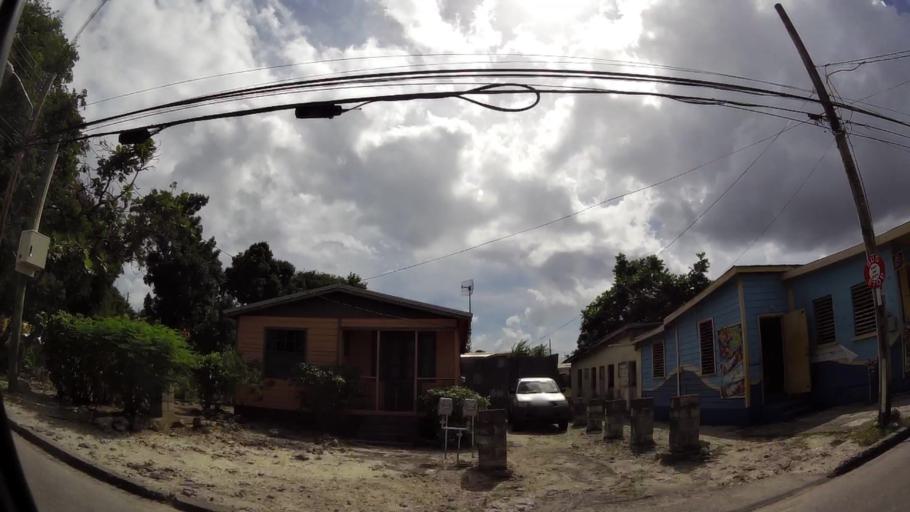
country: BB
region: Saint Michael
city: Bridgetown
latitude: 13.1112
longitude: -59.6234
